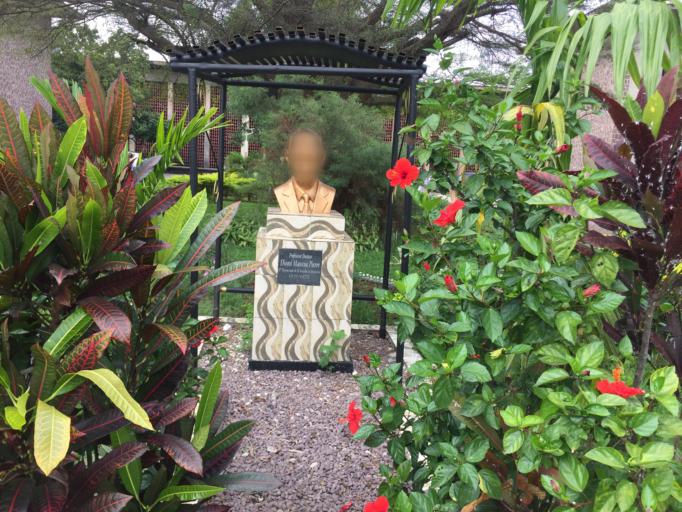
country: CD
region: Kinshasa
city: Kinshasa
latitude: -4.4165
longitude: 15.3070
